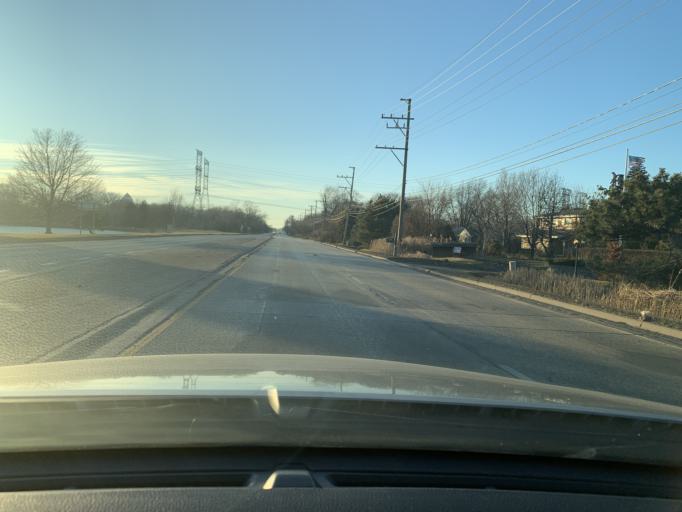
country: US
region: Illinois
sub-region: Cook County
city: Elk Grove Village
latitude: 41.9928
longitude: -87.9902
